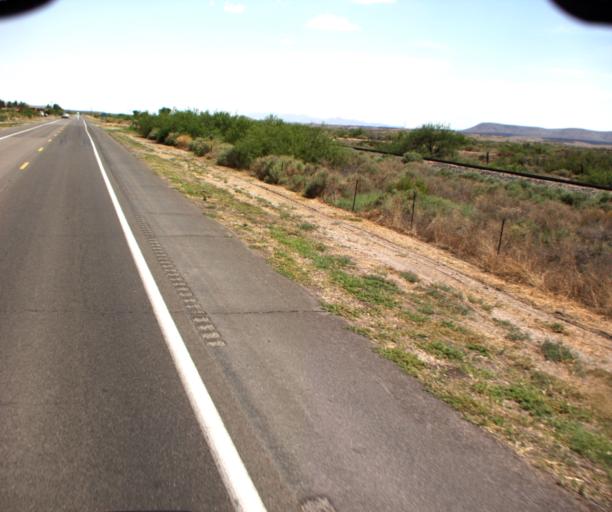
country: US
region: Arizona
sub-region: Greenlee County
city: Clifton
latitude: 32.6817
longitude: -109.0813
